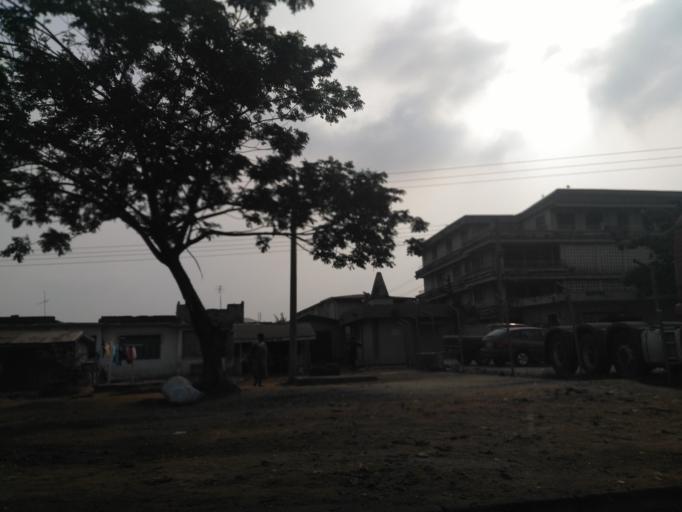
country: GH
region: Ashanti
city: Kumasi
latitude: 6.6957
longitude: -1.5927
